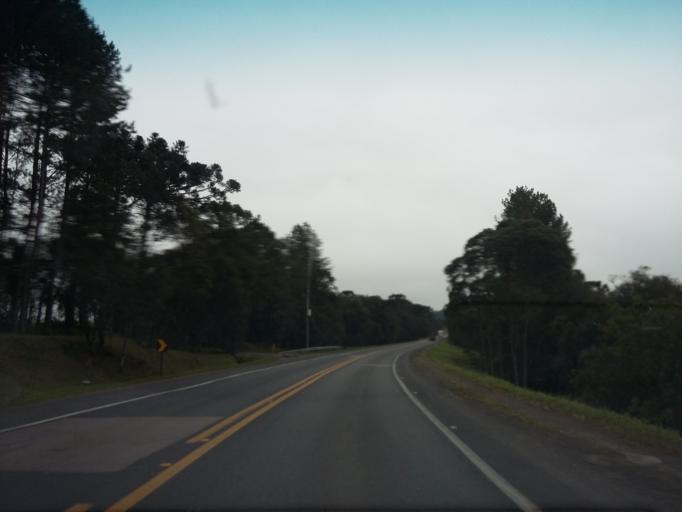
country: BR
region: Santa Catarina
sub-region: Santa Cecilia
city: Santa Cecilia
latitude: -26.6224
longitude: -50.2411
